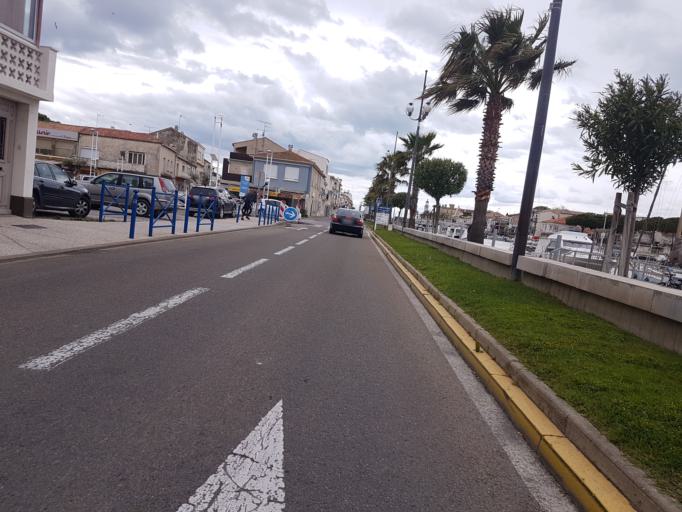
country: FR
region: Languedoc-Roussillon
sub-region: Departement du Gard
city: Le Grau-du-Roi
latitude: 43.5385
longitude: 4.1400
